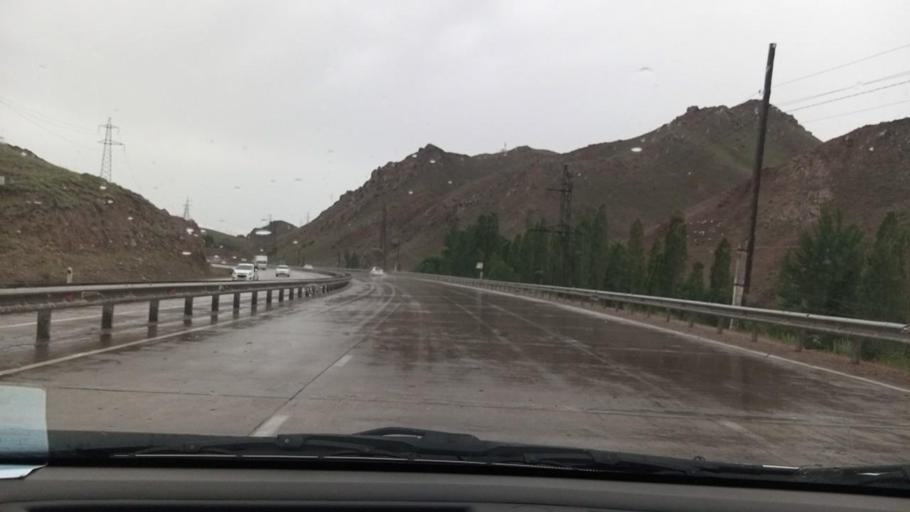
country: TJ
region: Viloyati Sughd
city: Shaydon
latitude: 40.9636
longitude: 70.6606
